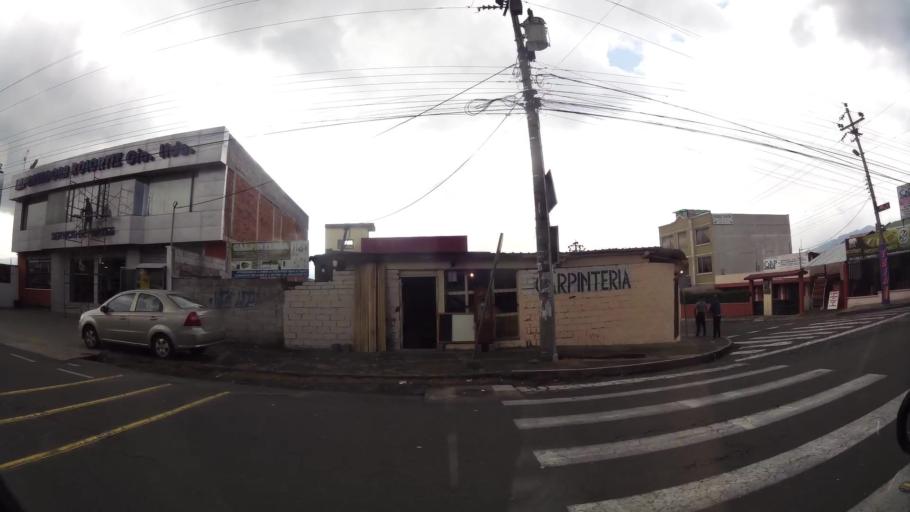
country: EC
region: Pichincha
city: Sangolqui
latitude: -0.3383
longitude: -78.4452
